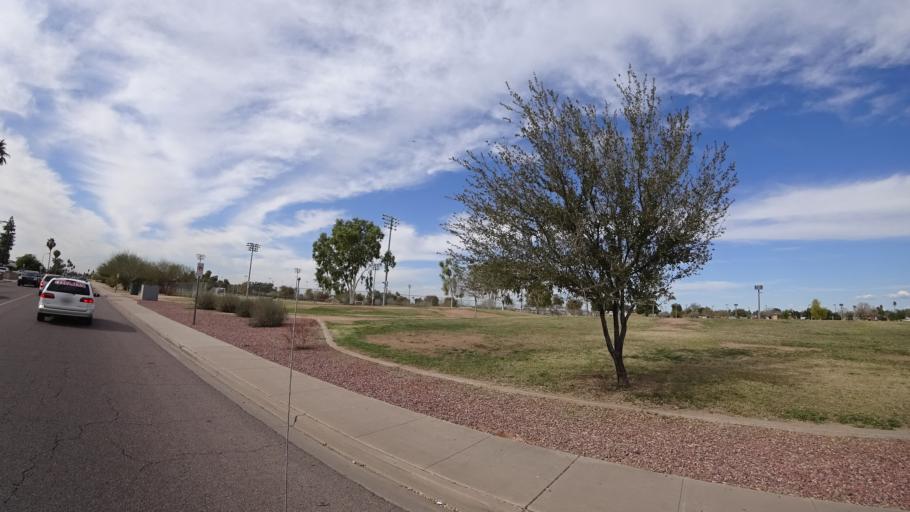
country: US
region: Arizona
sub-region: Maricopa County
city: Glendale
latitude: 33.4732
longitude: -112.1945
